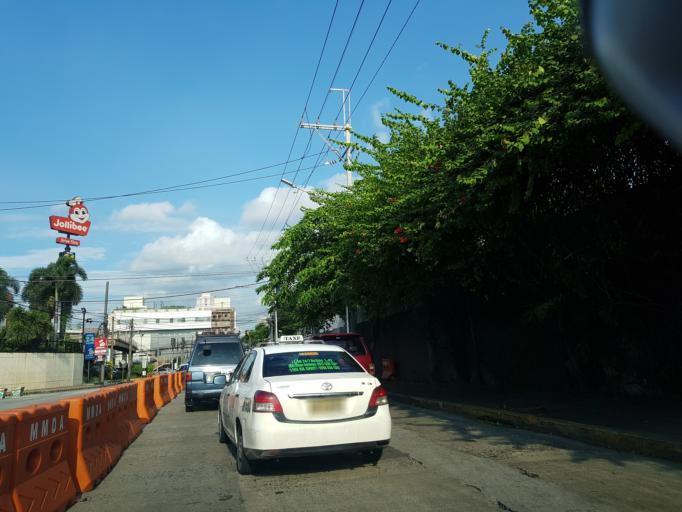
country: PH
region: Metro Manila
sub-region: Pasig
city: Pasig City
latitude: 14.6014
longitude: 121.0782
